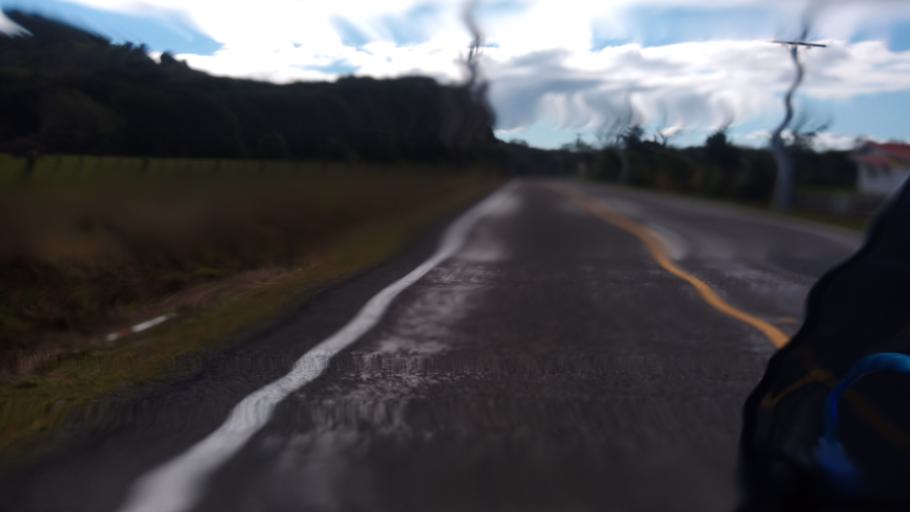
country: NZ
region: Gisborne
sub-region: Gisborne District
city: Gisborne
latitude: -37.9262
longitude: 178.2602
